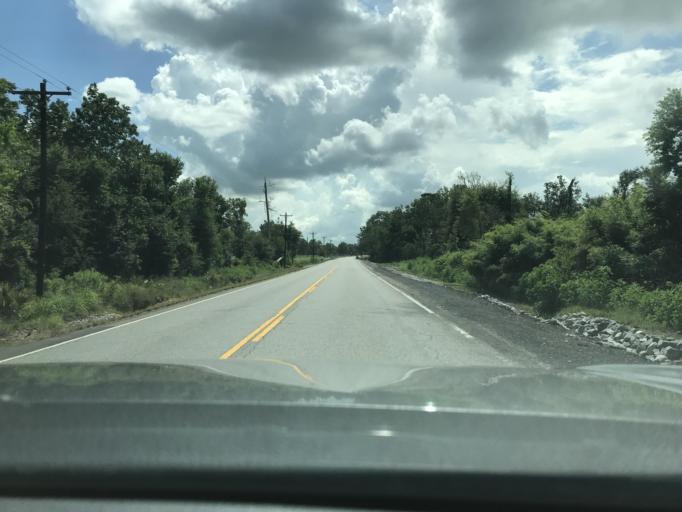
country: US
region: Louisiana
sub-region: Calcasieu Parish
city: Moss Bluff
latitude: 30.3396
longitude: -93.2564
